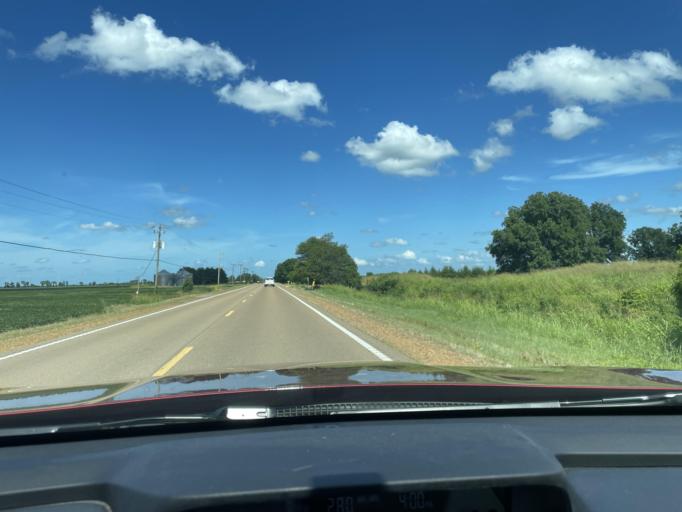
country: US
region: Mississippi
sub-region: Humphreys County
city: Belzoni
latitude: 33.1838
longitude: -90.5627
